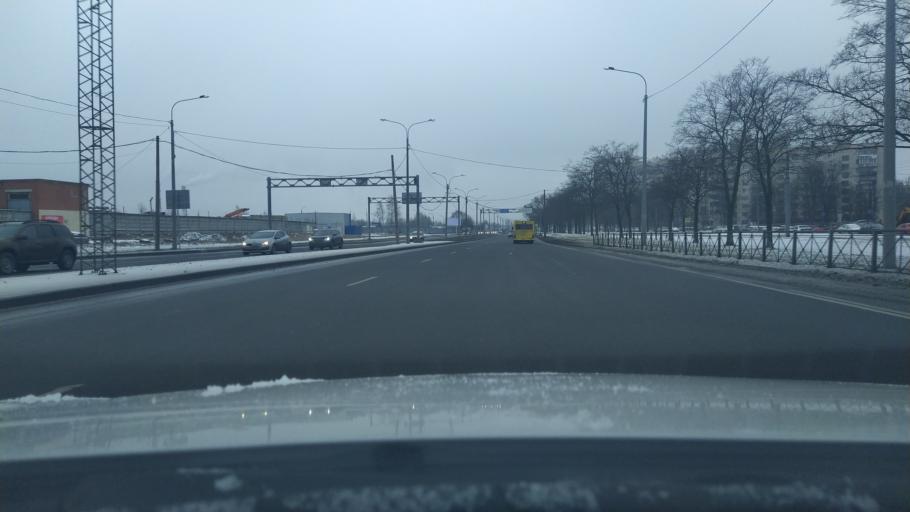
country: RU
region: Leningrad
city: Murino
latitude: 60.0389
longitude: 30.4324
